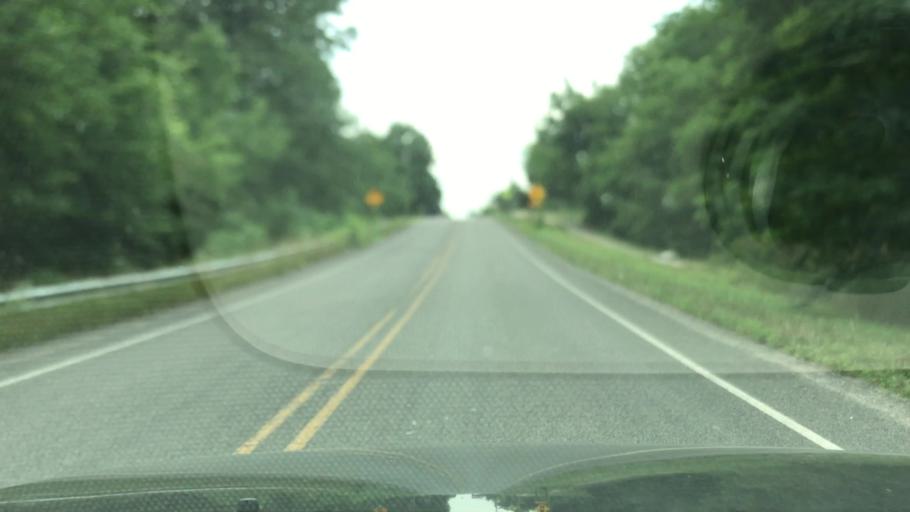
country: US
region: Michigan
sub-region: Kent County
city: East Grand Rapids
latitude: 42.9847
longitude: -85.5709
